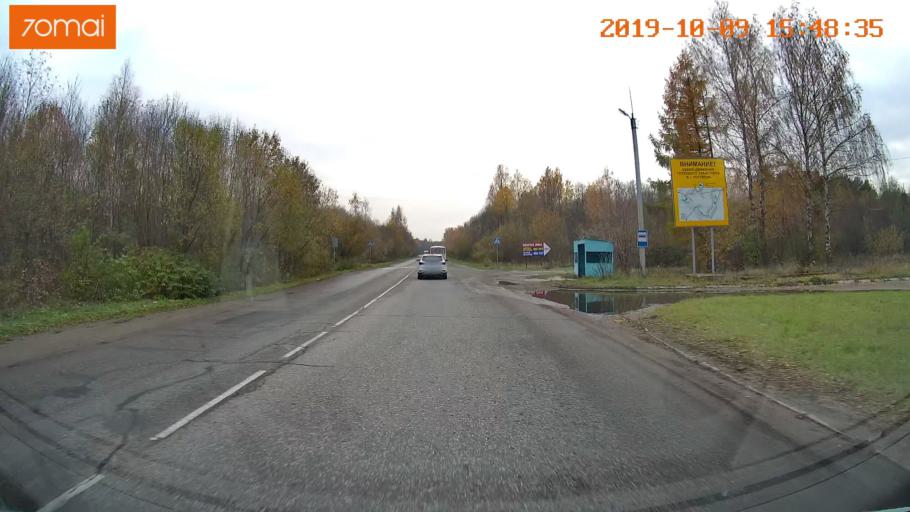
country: RU
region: Kostroma
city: Oktyabr'skiy
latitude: 57.8110
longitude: 41.0134
